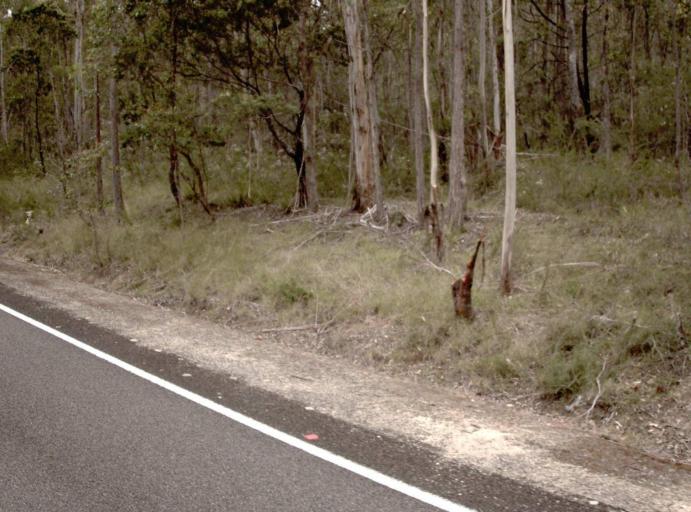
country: AU
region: New South Wales
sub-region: Bombala
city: Bombala
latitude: -37.2804
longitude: 149.2234
